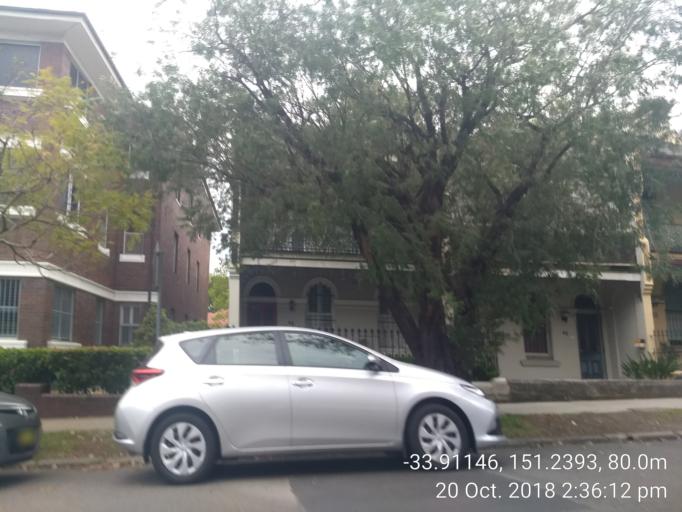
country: AU
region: New South Wales
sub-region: Randwick
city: Randwick
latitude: -33.9115
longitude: 151.2393
